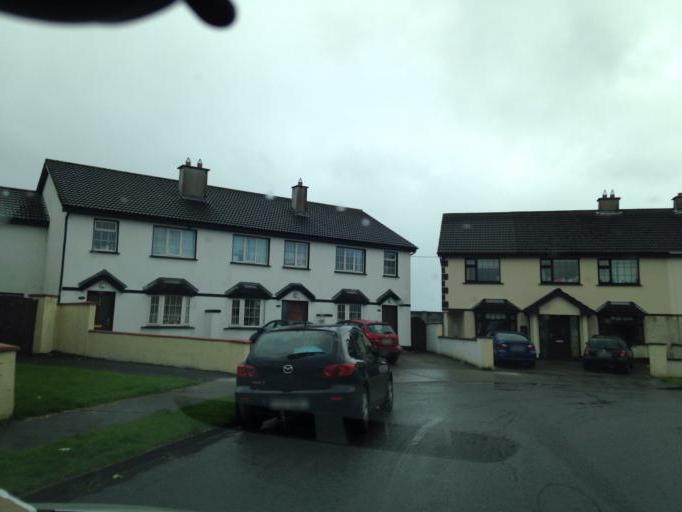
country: IE
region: Connaught
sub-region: County Galway
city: Gaillimh
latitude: 53.2730
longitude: -9.0055
